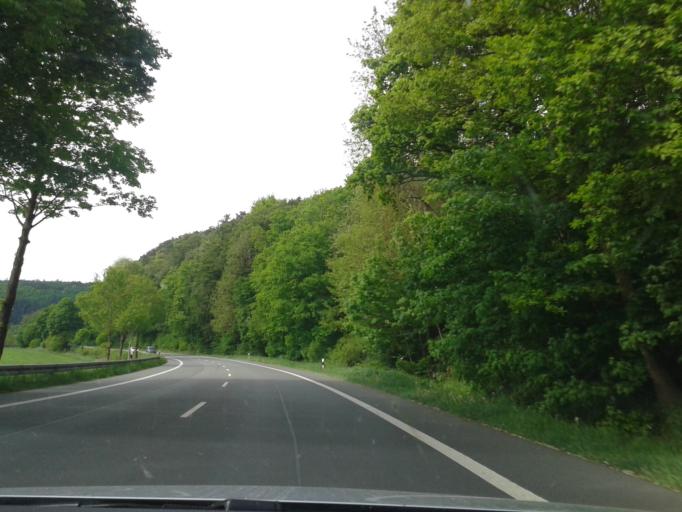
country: DE
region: Hesse
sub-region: Regierungsbezirk Kassel
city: Frankenau
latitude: 51.1204
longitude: 8.8760
